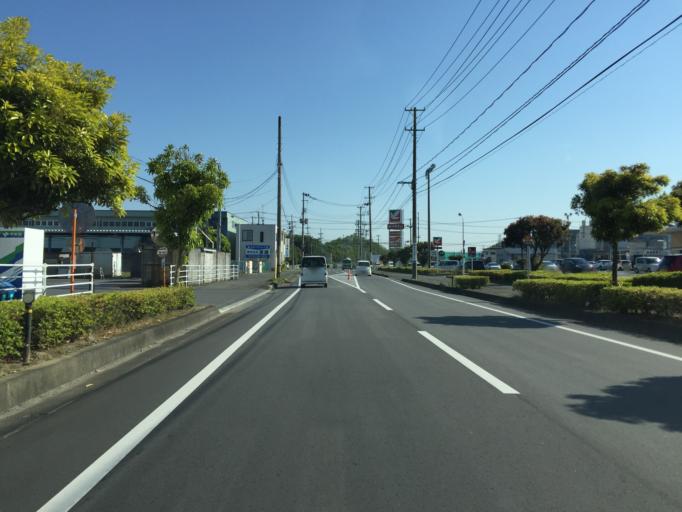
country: JP
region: Ibaraki
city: Kitaibaraki
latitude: 36.9085
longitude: 140.7730
